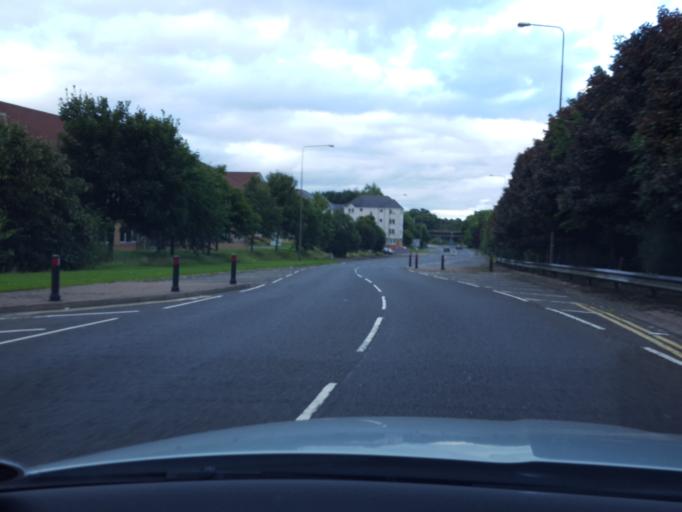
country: GB
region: Scotland
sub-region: West Lothian
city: Livingston
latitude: 55.8849
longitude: -3.5054
